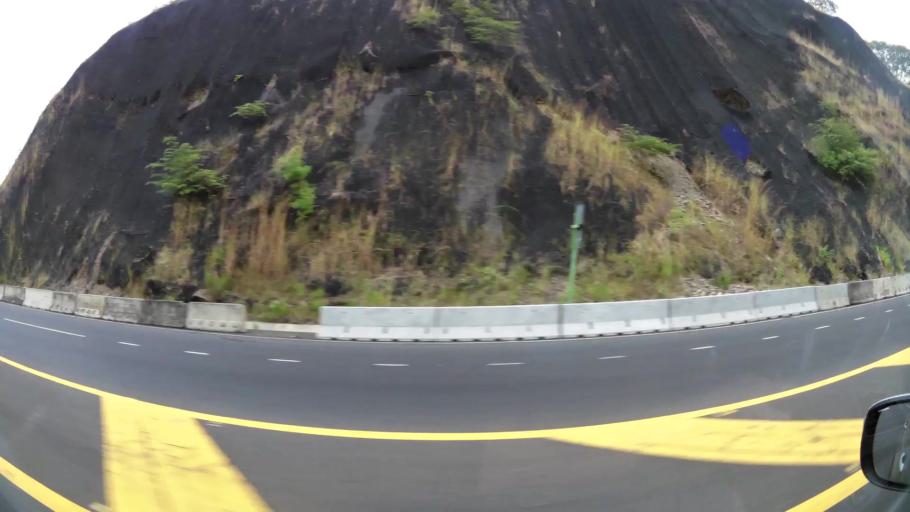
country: CR
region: Alajuela
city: Atenas
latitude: 9.9391
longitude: -84.4003
